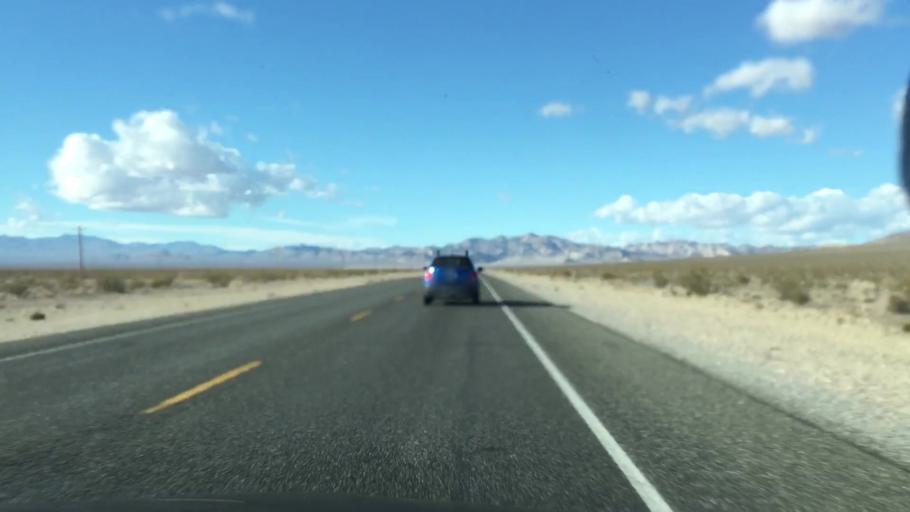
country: US
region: Nevada
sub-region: Nye County
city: Beatty
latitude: 36.7990
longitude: -116.7147
